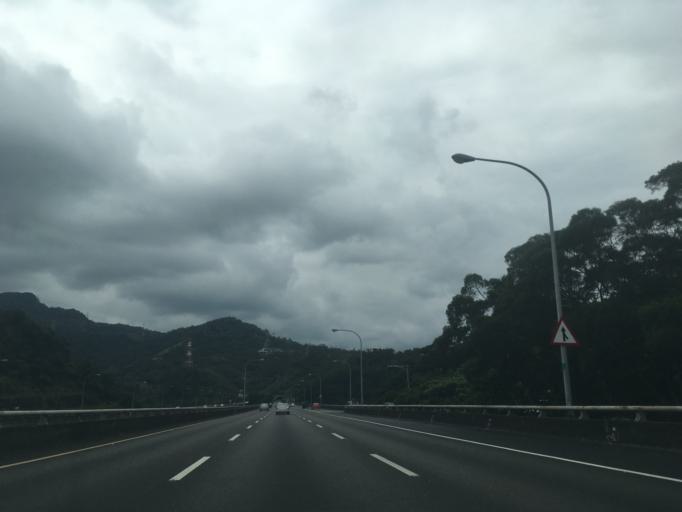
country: TW
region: Taipei
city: Taipei
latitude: 25.0010
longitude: 121.5946
